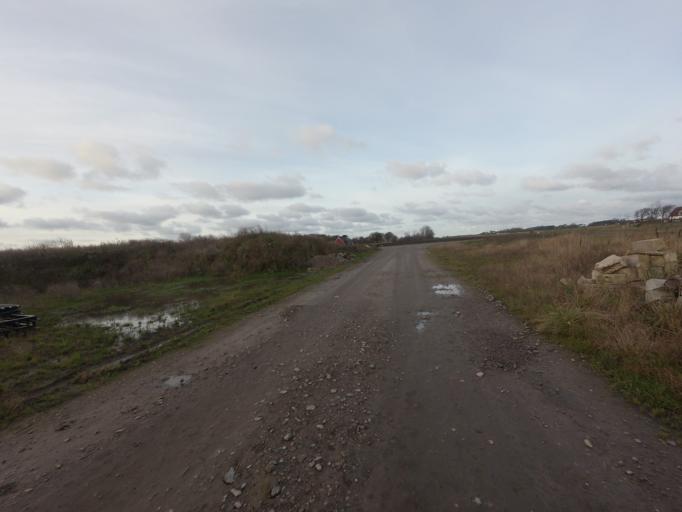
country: SE
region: Skane
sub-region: Hoganas Kommun
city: Hoganas
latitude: 56.1628
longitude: 12.5798
